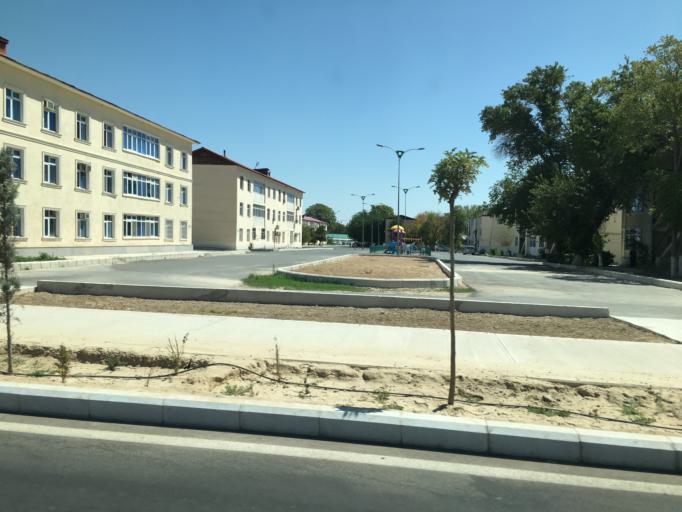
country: TM
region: Ahal
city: Ashgabat
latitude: 37.9270
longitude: 58.3915
